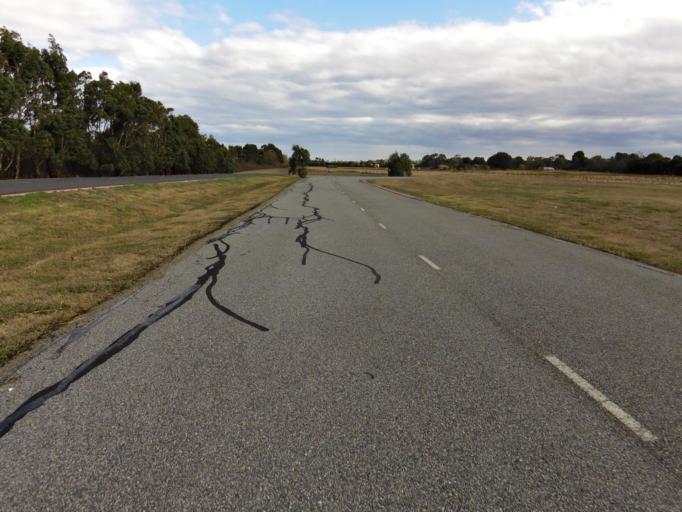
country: AU
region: Victoria
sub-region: Casey
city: Junction Village
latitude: -38.1272
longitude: 145.3157
